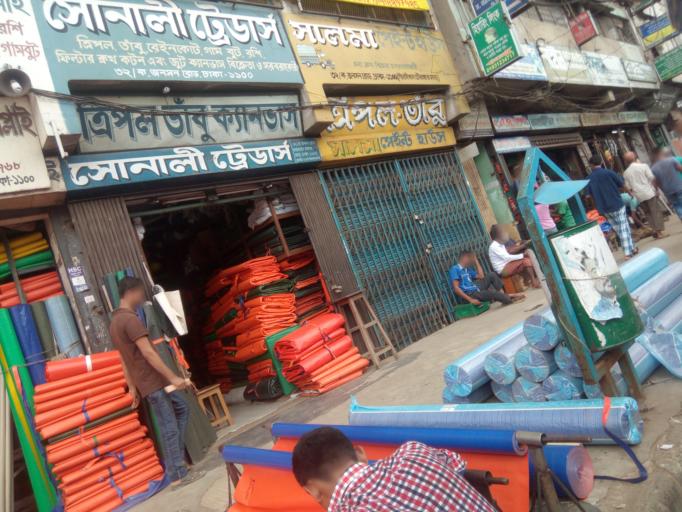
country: BD
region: Dhaka
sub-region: Dhaka
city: Dhaka
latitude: 23.7137
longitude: 90.4118
